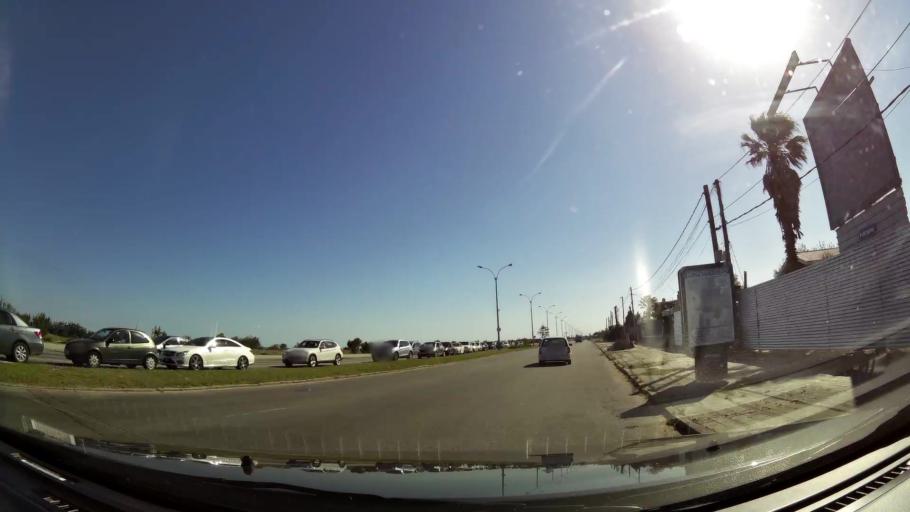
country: UY
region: Canelones
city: Barra de Carrasco
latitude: -34.8821
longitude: -56.0355
